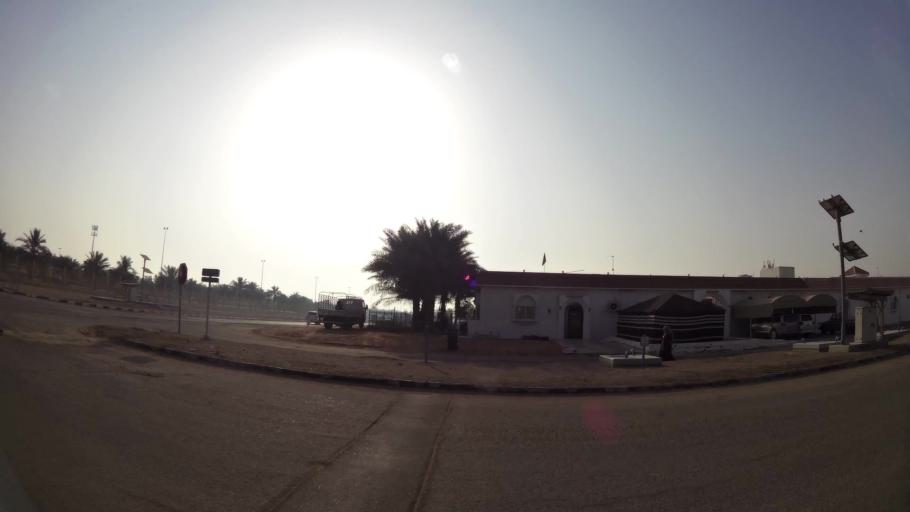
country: AE
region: Abu Dhabi
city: Abu Dhabi
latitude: 24.2880
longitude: 54.6375
